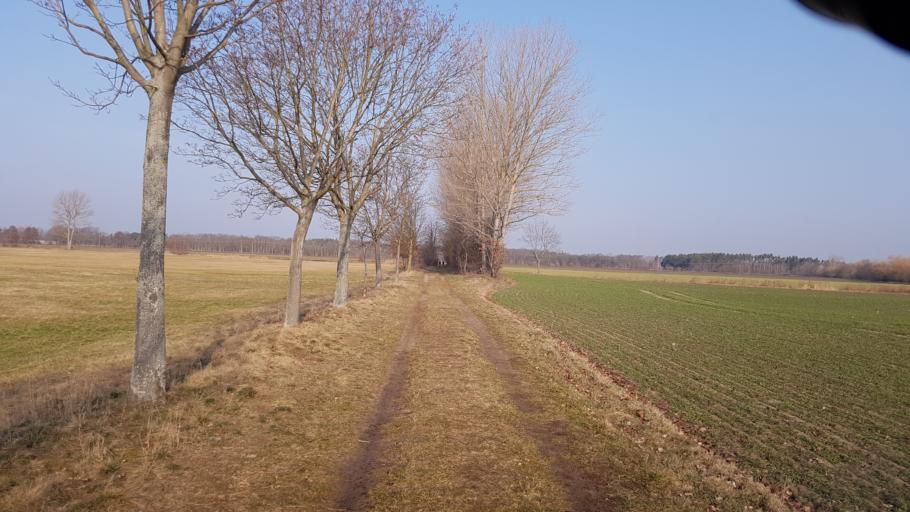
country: DE
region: Brandenburg
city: Falkenberg
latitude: 51.5929
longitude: 13.2833
